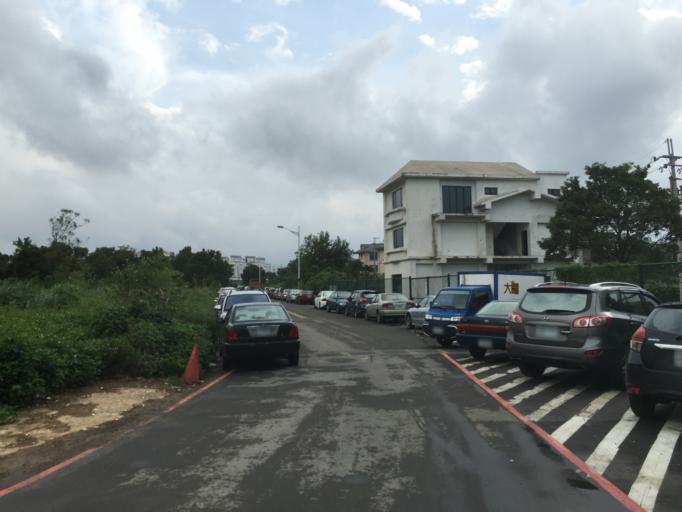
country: TW
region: Taiwan
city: Daxi
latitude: 24.8712
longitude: 121.2311
